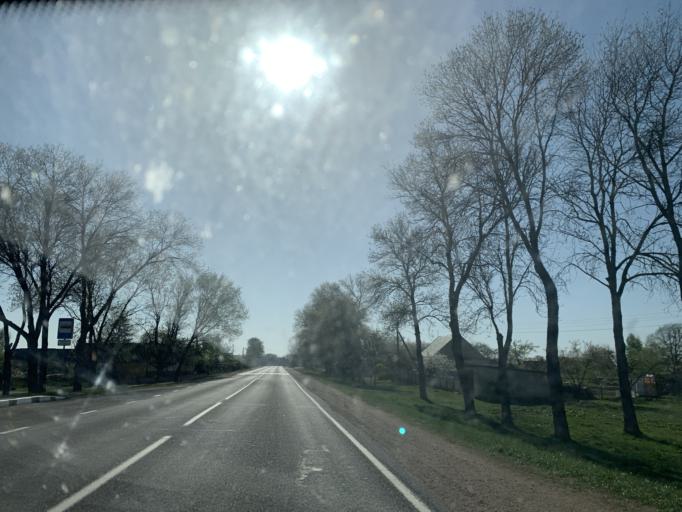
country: BY
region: Minsk
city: Nyasvizh
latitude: 53.2285
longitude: 26.7206
